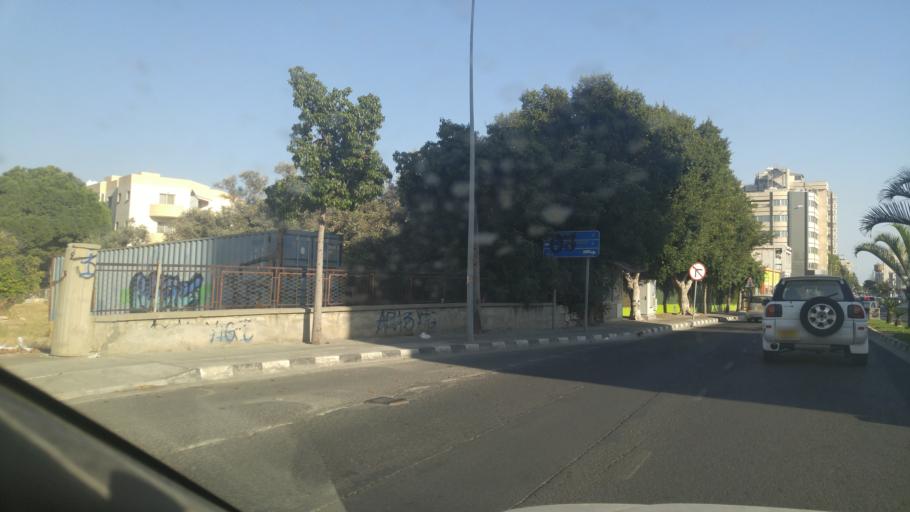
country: CY
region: Limassol
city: Limassol
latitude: 34.6841
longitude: 33.0292
